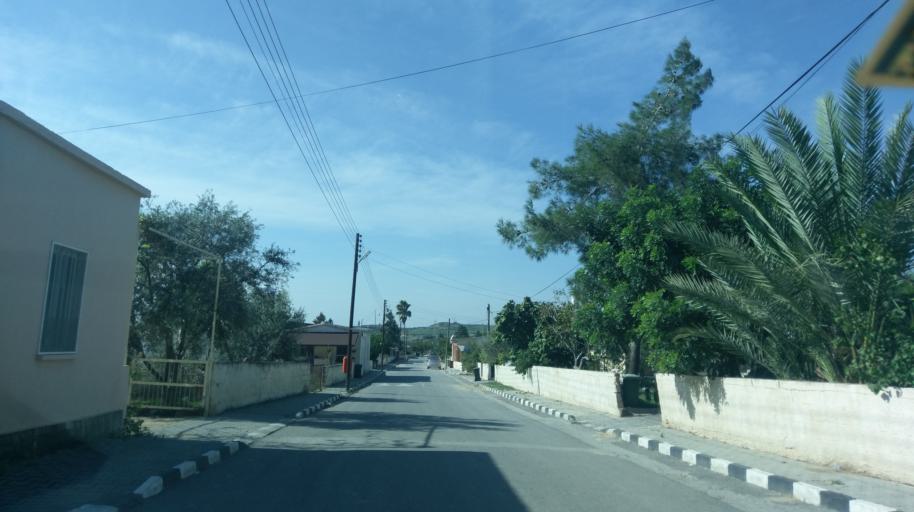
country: CY
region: Ammochostos
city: Trikomo
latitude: 35.3430
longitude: 33.9985
